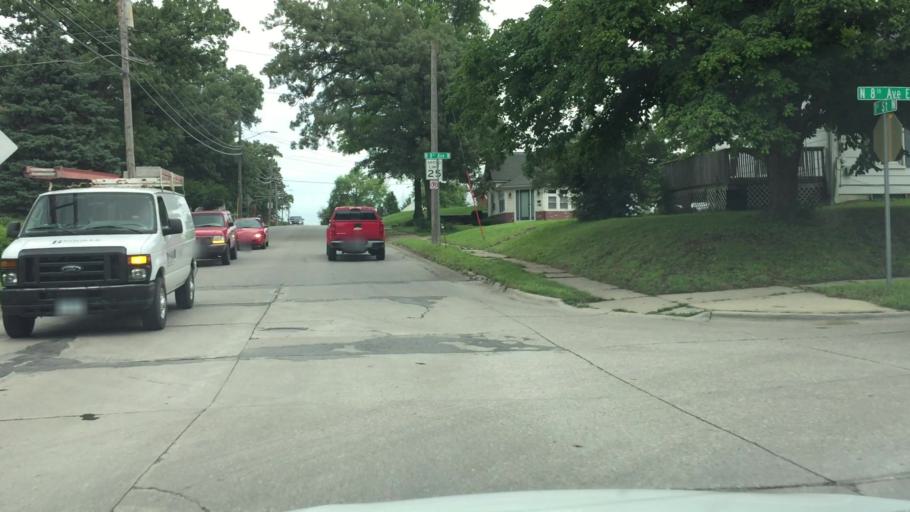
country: US
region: Iowa
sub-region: Jasper County
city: Newton
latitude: 41.7063
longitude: -93.0532
